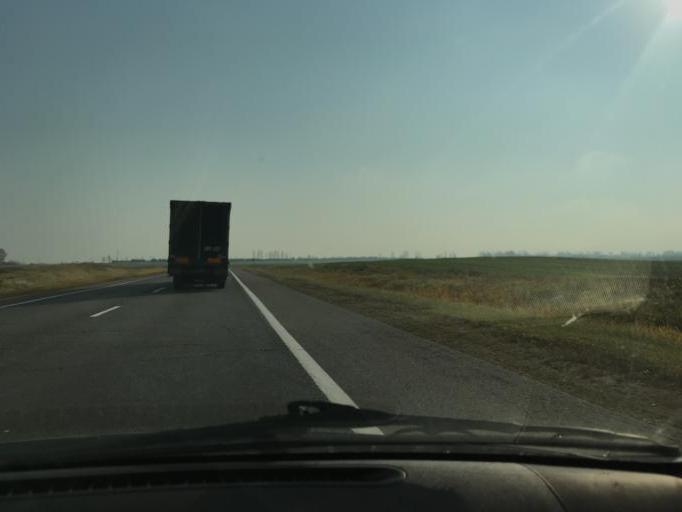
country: BY
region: Vitebsk
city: Chashniki
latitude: 55.0094
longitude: 29.1292
